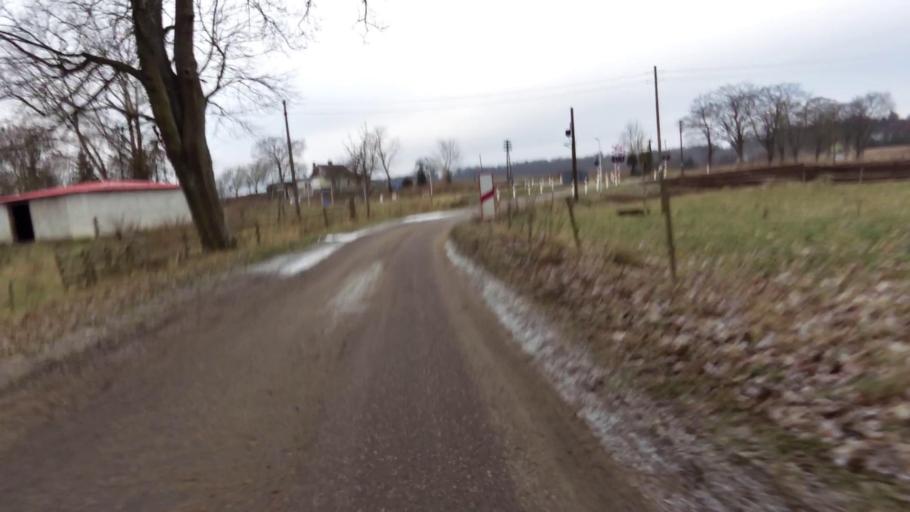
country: PL
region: West Pomeranian Voivodeship
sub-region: Powiat szczecinecki
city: Szczecinek
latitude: 53.6591
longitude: 16.6269
